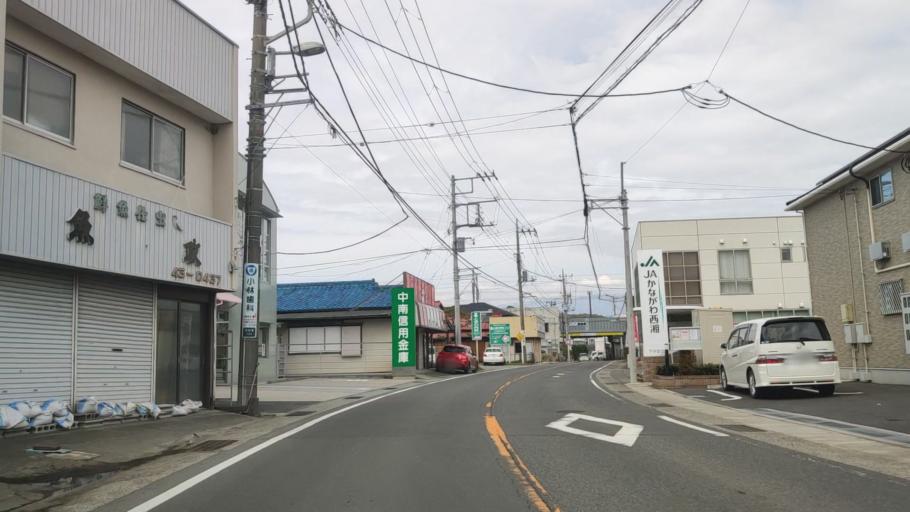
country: JP
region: Kanagawa
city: Ninomiya
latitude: 35.3000
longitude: 139.2284
